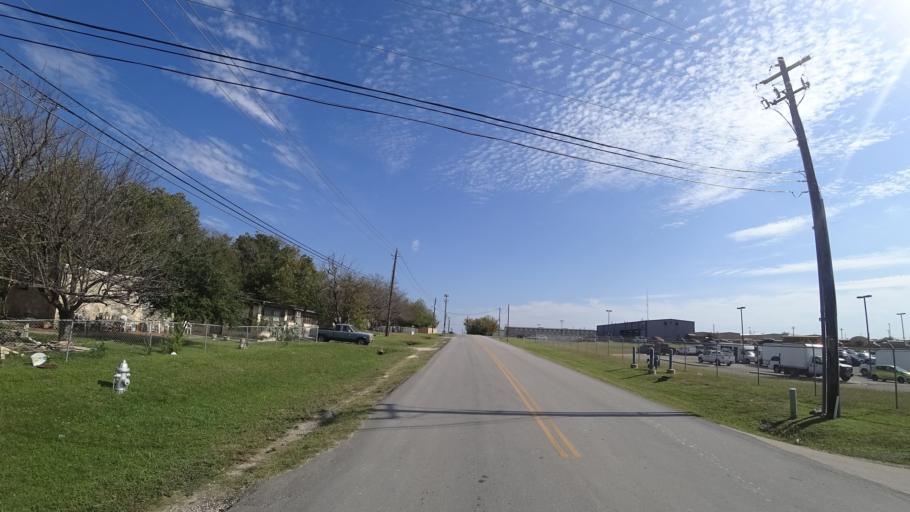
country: US
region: Texas
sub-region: Travis County
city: Pflugerville
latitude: 30.4067
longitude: -97.6307
